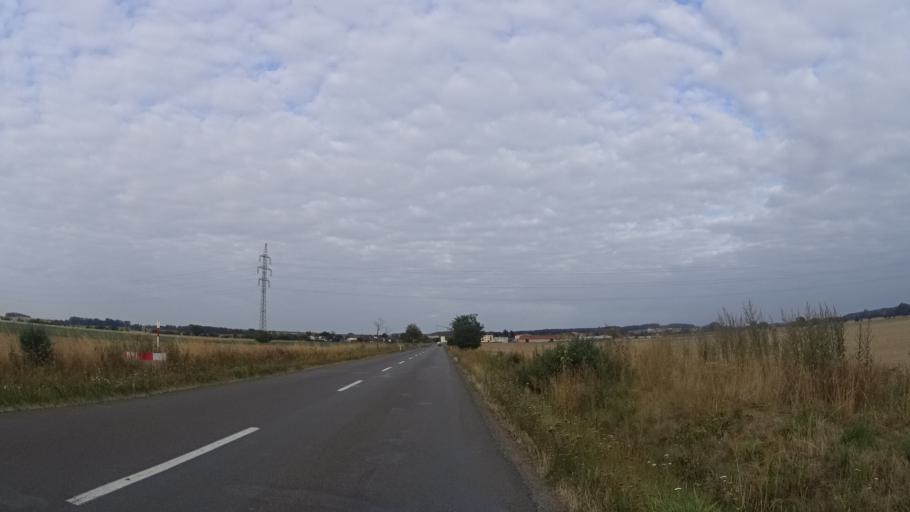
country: CZ
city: Stezery
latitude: 50.2114
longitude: 15.7687
